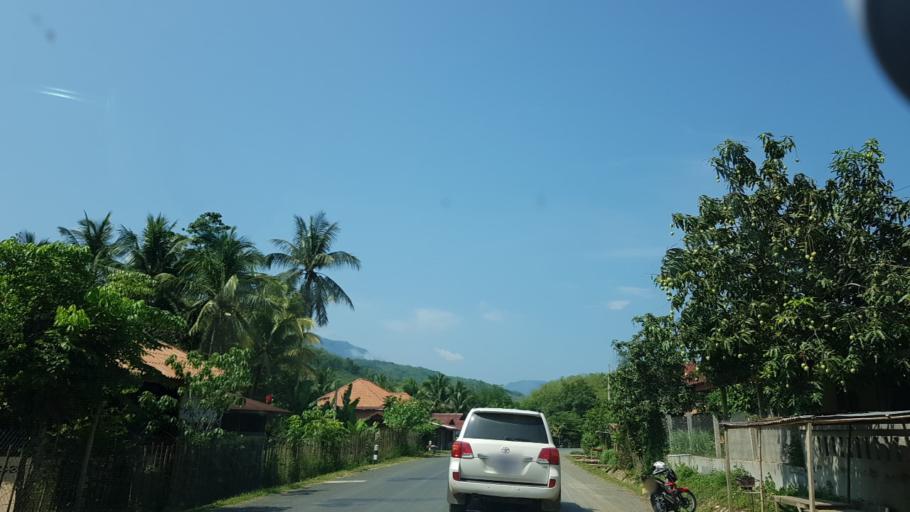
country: LA
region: Louangphabang
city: Xiang Ngeun
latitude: 19.7302
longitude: 102.1542
